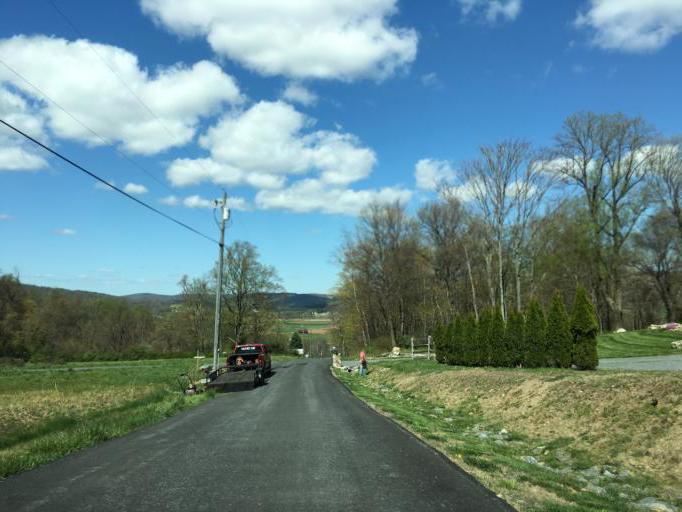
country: US
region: Maryland
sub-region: Washington County
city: Highfield-Cascade
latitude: 39.6691
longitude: -77.4702
